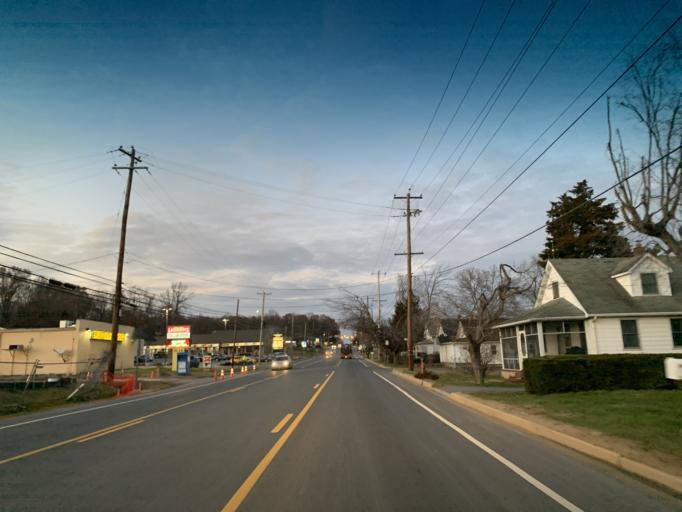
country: US
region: Maryland
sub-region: Cecil County
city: Elkton
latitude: 39.6163
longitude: -75.8380
